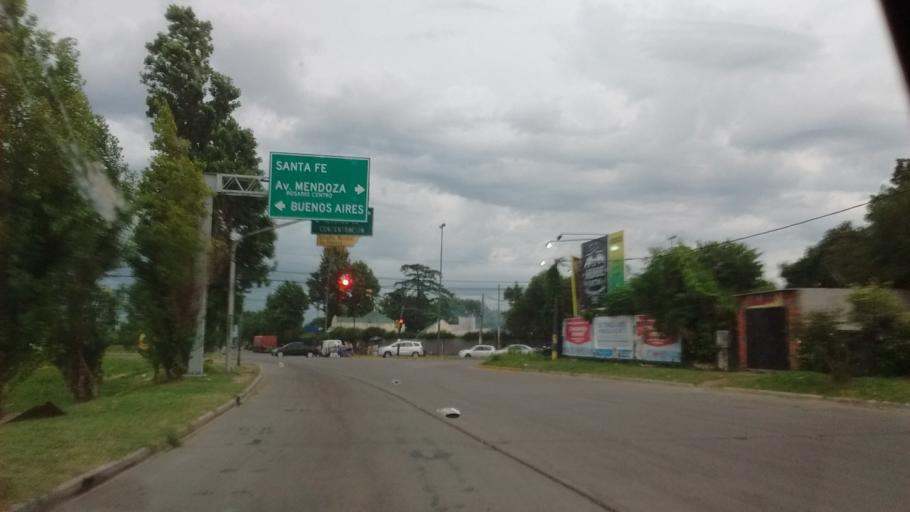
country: AR
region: Santa Fe
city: Perez
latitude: -32.9411
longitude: -60.7218
